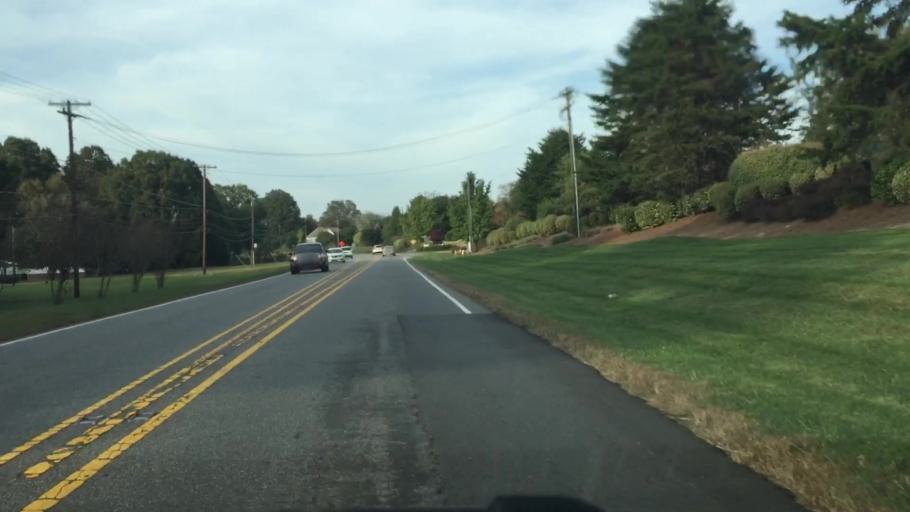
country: US
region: North Carolina
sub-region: Iredell County
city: Mooresville
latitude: 35.5717
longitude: -80.7921
